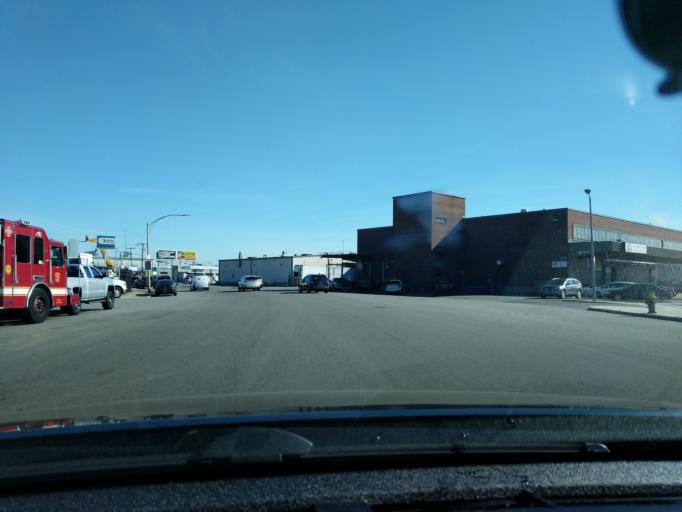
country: US
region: Massachusetts
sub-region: Suffolk County
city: South Boston
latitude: 42.3305
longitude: -71.0690
